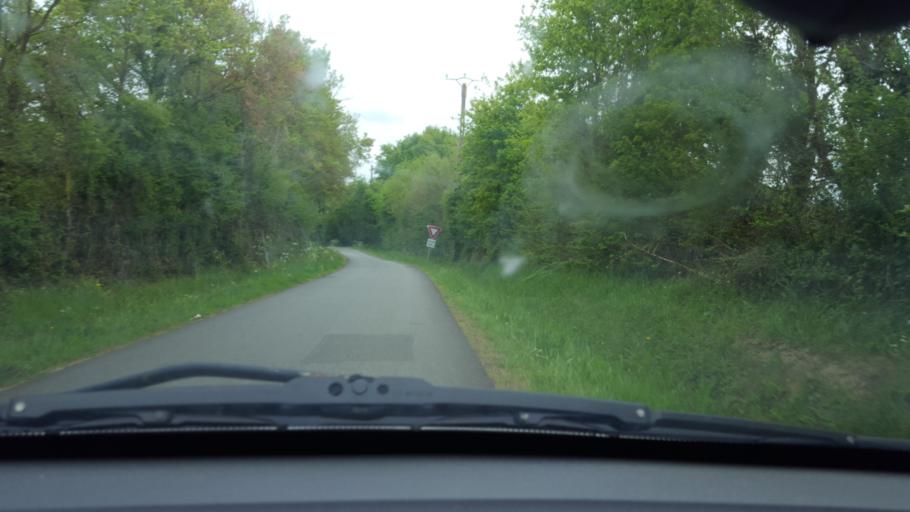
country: FR
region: Pays de la Loire
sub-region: Departement de la Loire-Atlantique
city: La Limouziniere
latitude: 47.0241
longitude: -1.5987
